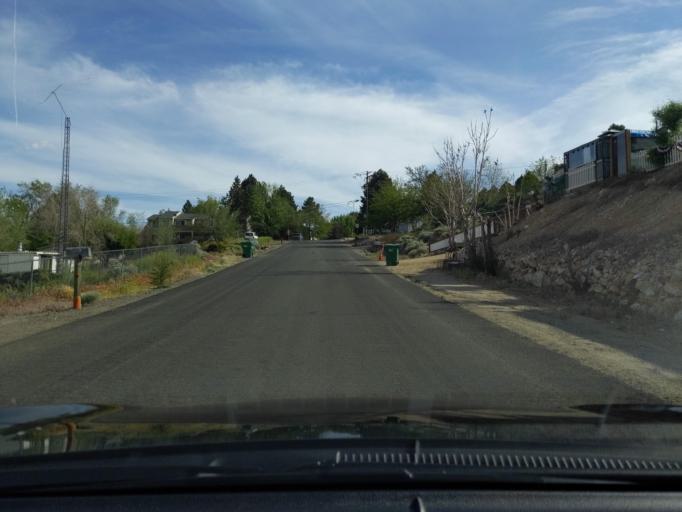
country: US
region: Nevada
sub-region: Washoe County
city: Sun Valley
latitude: 39.5684
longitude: -119.7832
